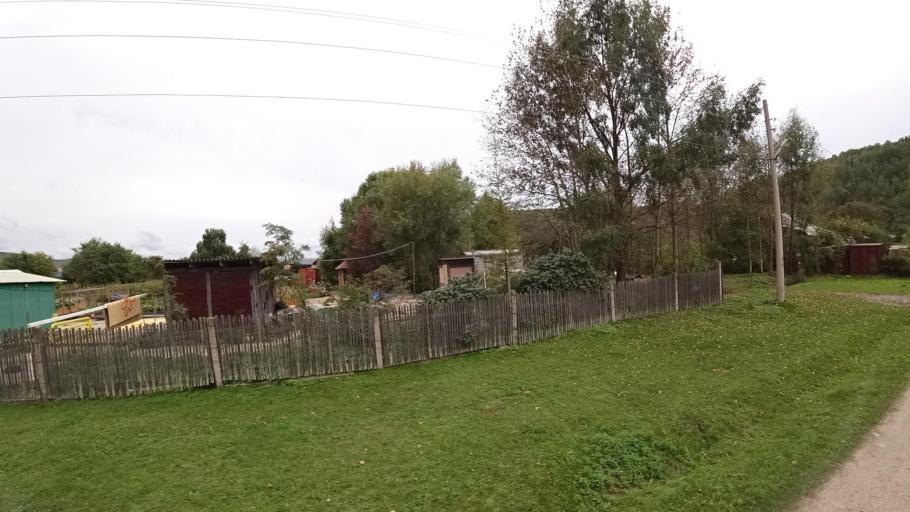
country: RU
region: Jewish Autonomous Oblast
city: Khingansk
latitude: 49.0339
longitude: 131.0475
